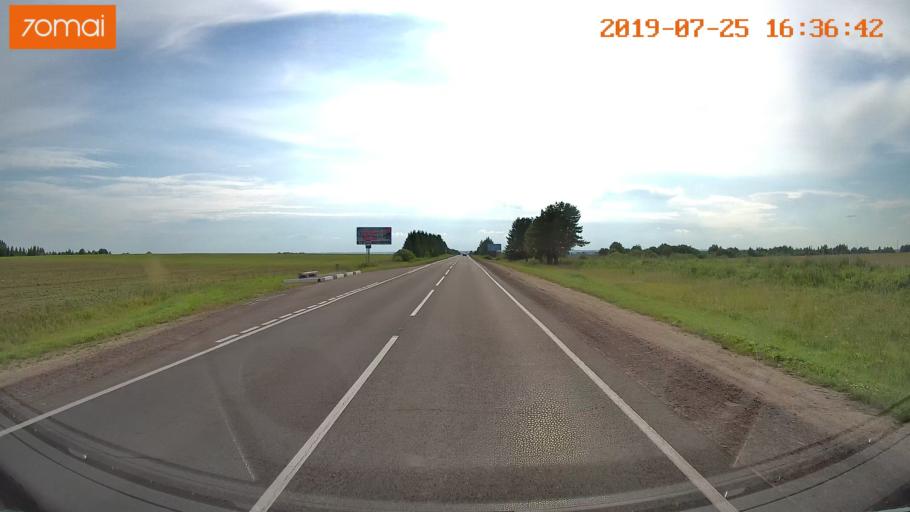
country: RU
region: Ivanovo
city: Privolzhsk
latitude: 57.3947
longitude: 41.3953
